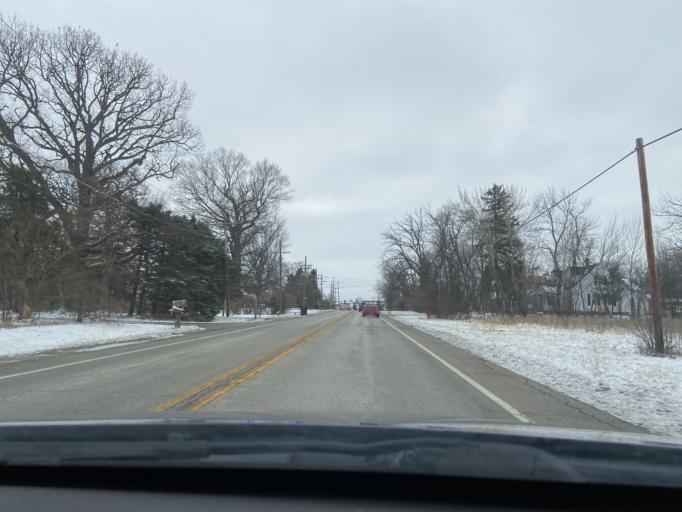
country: US
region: Illinois
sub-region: Lake County
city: Round Lake Park
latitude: 42.3598
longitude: -88.0680
